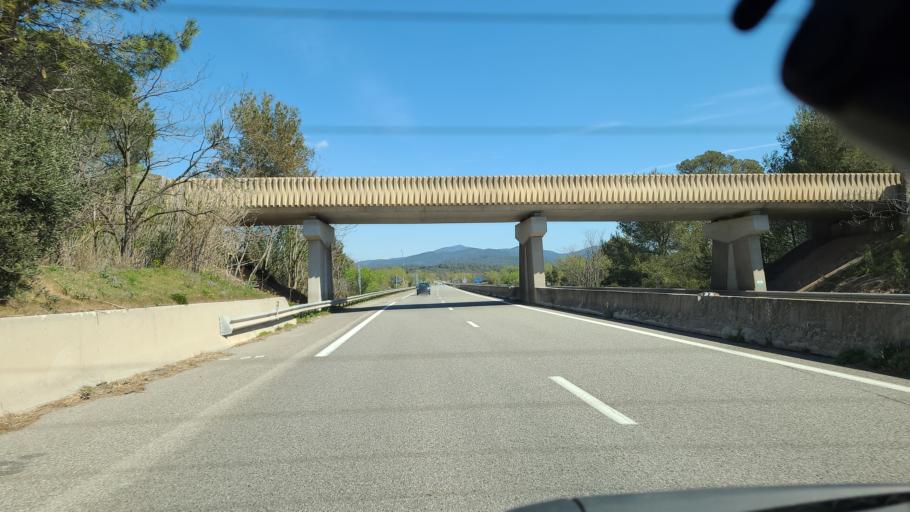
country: FR
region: Provence-Alpes-Cote d'Azur
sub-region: Departement du Var
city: Cuers
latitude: 43.2519
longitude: 6.1007
